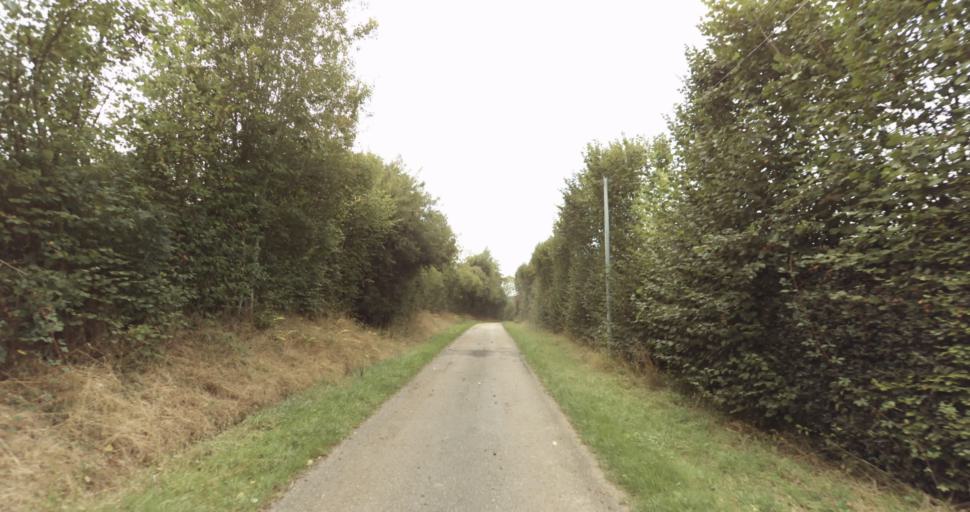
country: FR
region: Lower Normandy
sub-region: Departement de l'Orne
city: Sainte-Gauburge-Sainte-Colombe
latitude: 48.7639
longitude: 0.3774
